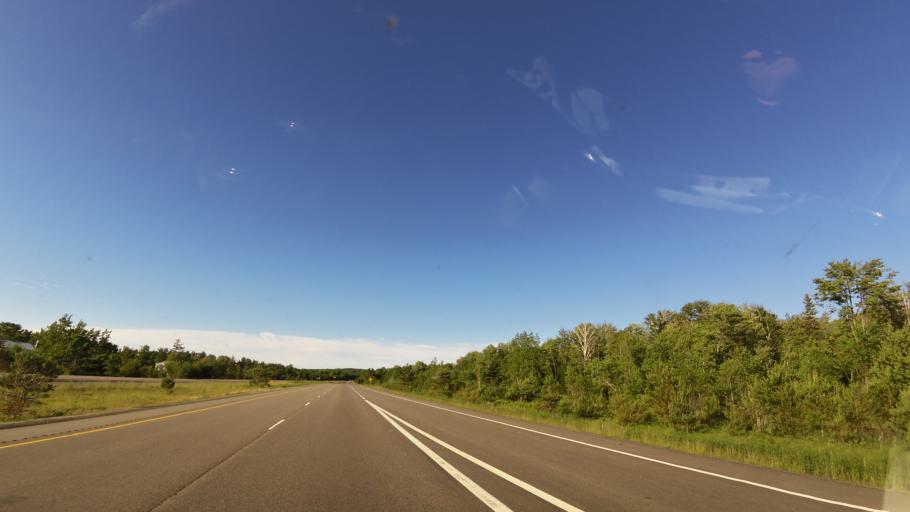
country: CA
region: Ontario
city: Barrie
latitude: 44.5545
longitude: -79.7431
